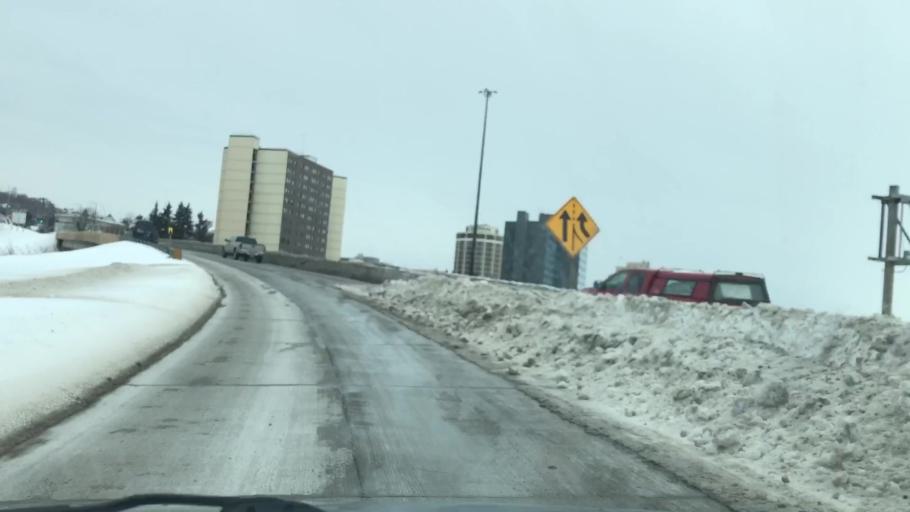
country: US
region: Minnesota
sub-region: Saint Louis County
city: Duluth
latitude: 46.7785
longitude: -92.1080
